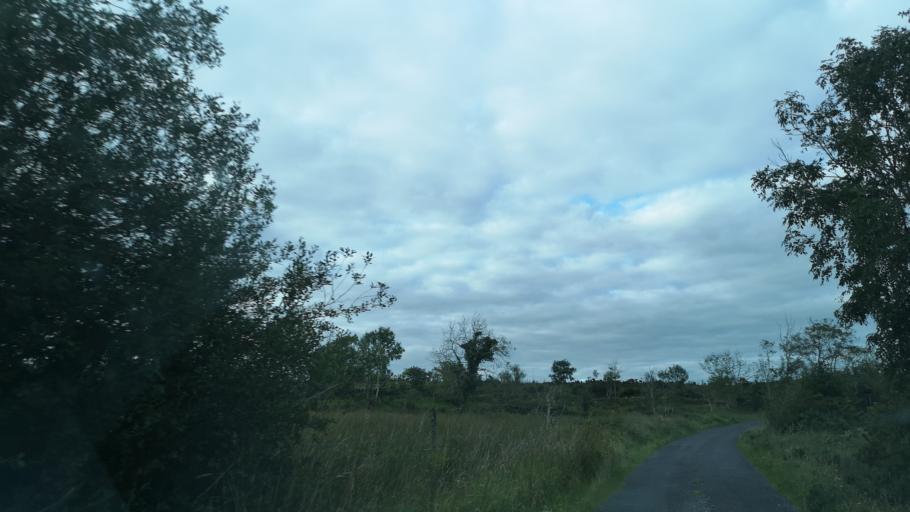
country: IE
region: Connaught
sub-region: County Galway
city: Loughrea
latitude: 53.1314
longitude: -8.5224
